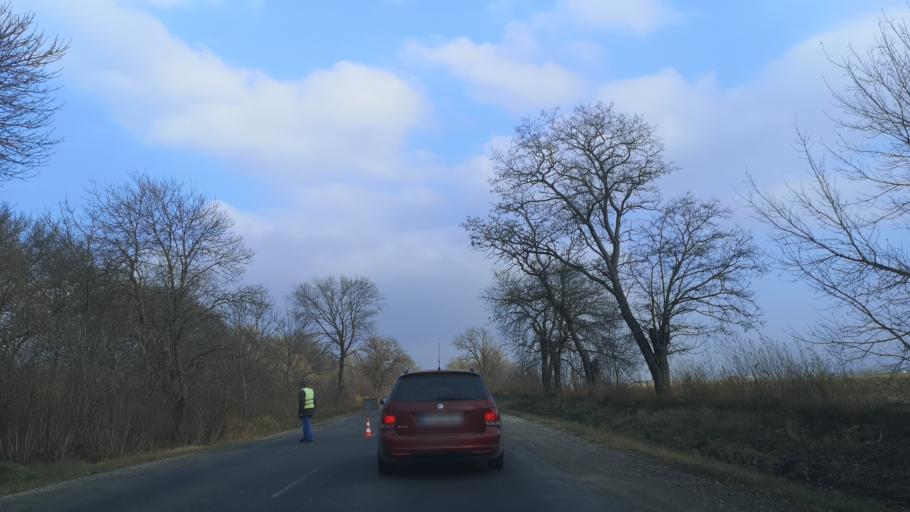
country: MD
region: Balti
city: Balti
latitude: 47.7857
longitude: 27.9787
